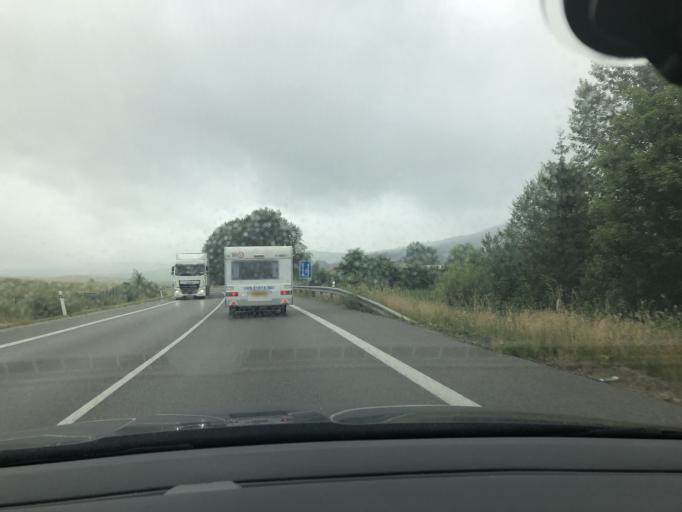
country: SK
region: Zilinsky
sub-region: Okres Zilina
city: Trstena
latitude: 49.3524
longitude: 19.6121
